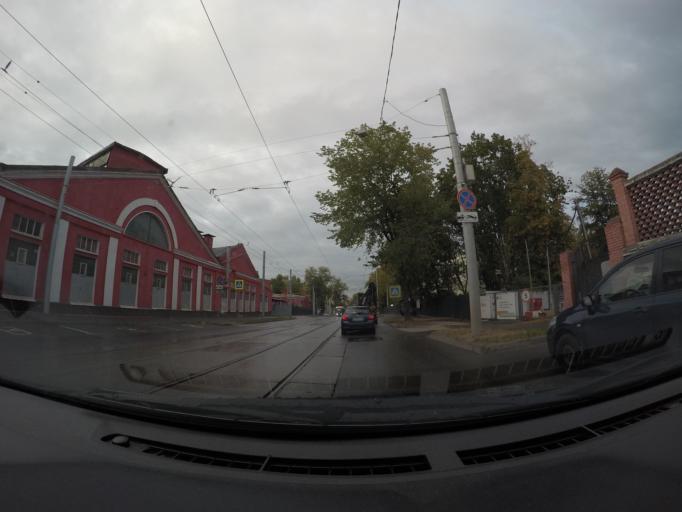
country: RU
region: Moscow
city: Lefortovo
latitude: 55.7893
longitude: 37.6936
